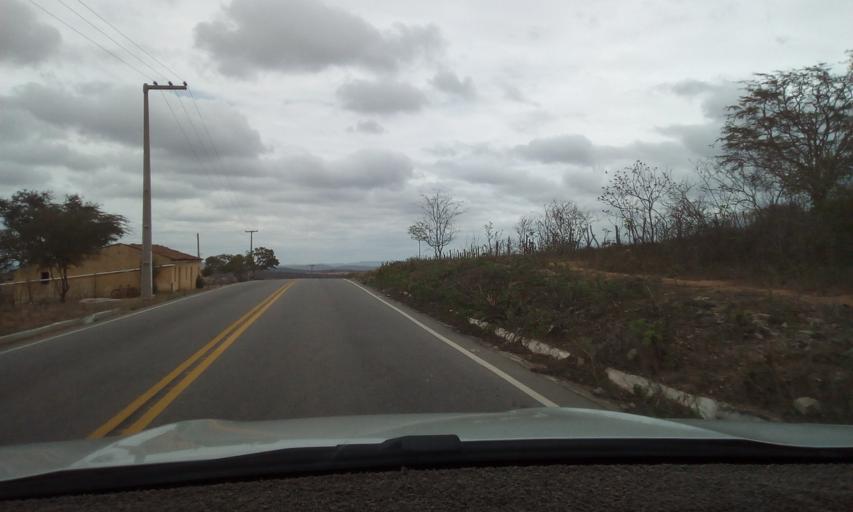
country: BR
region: Paraiba
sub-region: Picui
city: Picui
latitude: -6.5726
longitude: -36.2693
